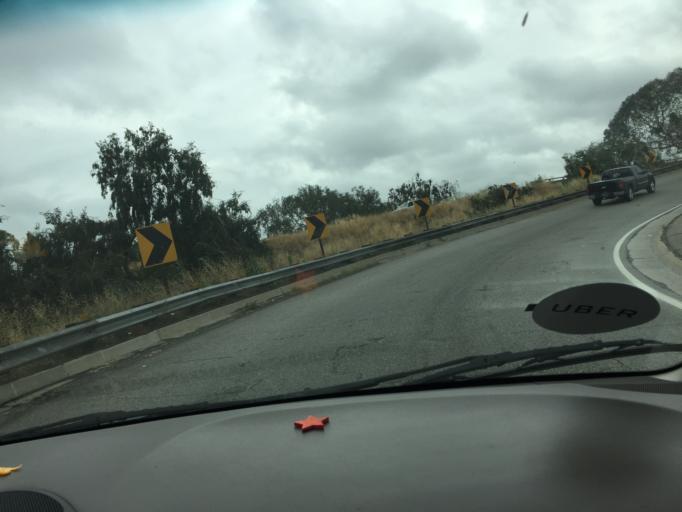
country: US
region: California
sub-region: Los Angeles County
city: Signal Hill
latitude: 33.8276
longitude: -118.2071
